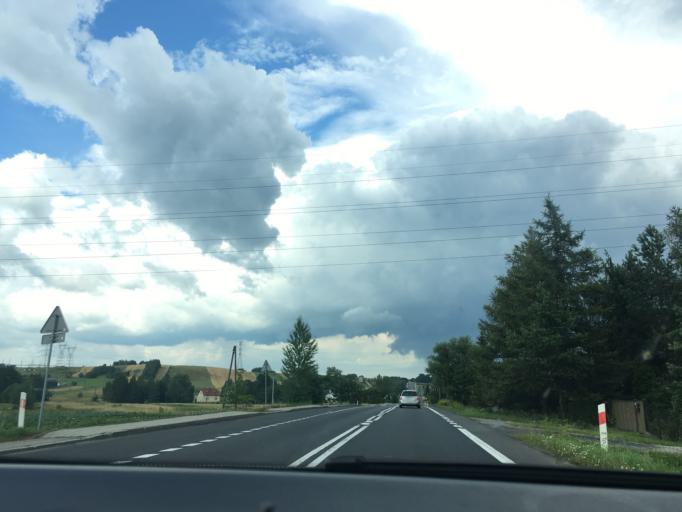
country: PL
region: Subcarpathian Voivodeship
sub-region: Powiat krosnienski
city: Kroscienko Wyzne
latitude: 49.6802
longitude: 21.8507
